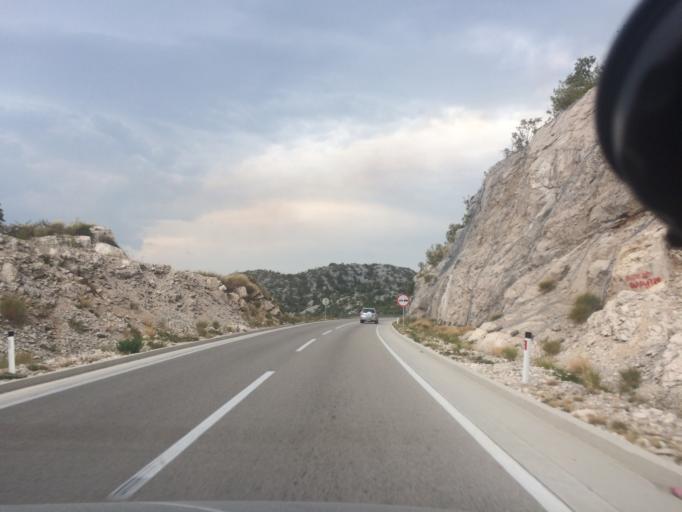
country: ME
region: Kotor
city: Risan
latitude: 42.6314
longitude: 18.6812
